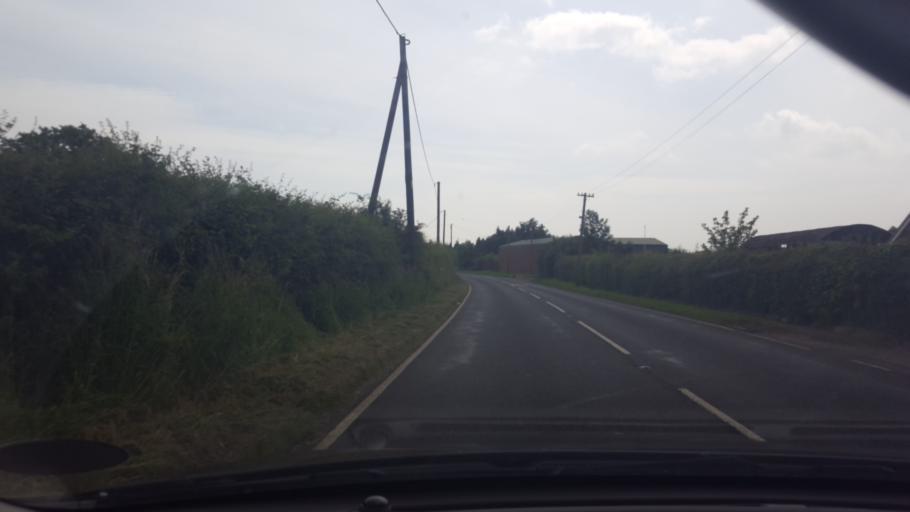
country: GB
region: England
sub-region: Essex
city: Mistley
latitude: 51.8933
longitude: 1.1031
